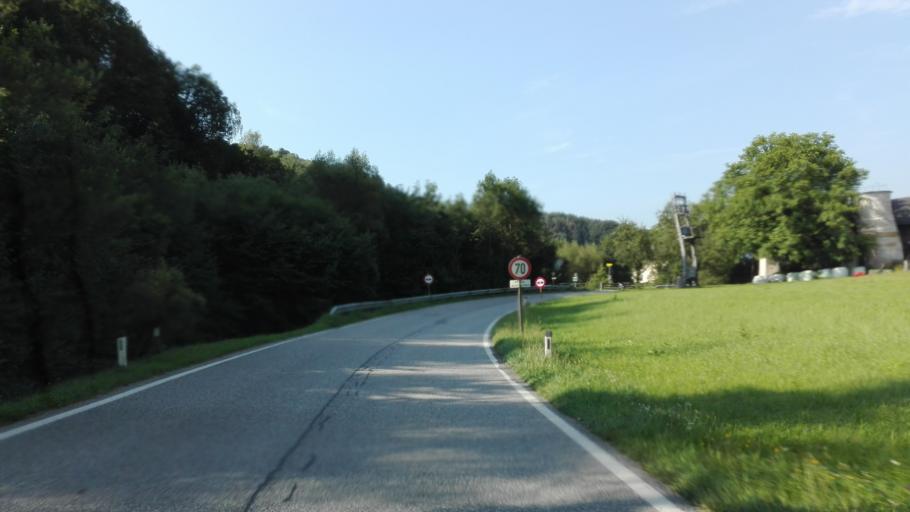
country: AT
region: Lower Austria
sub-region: Politischer Bezirk Lilienfeld
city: Eschenau
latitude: 48.0636
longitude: 15.5914
